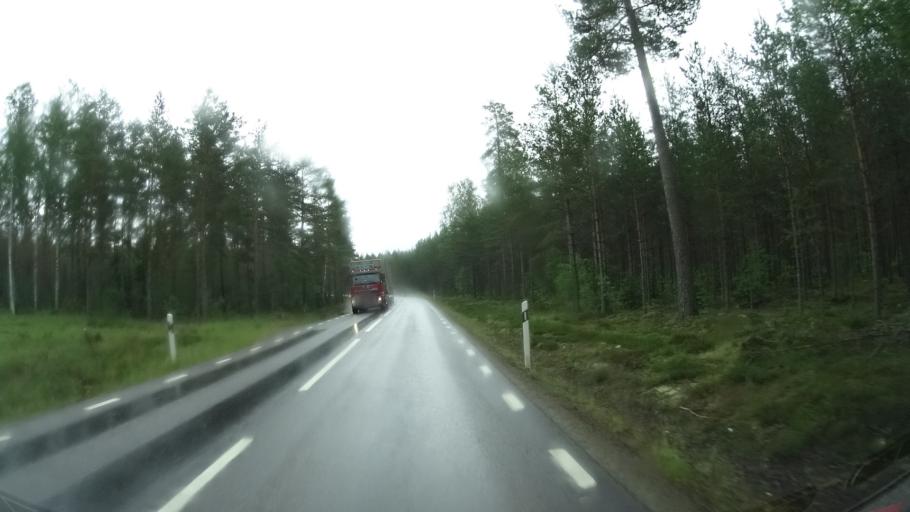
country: SE
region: Kalmar
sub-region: Hultsfreds Kommun
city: Hultsfred
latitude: 57.5167
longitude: 15.8118
